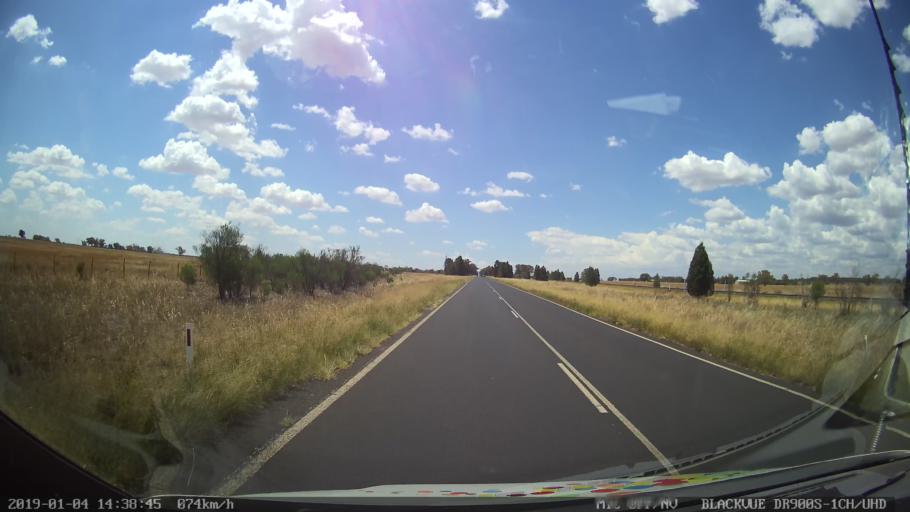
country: AU
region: New South Wales
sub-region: Dubbo Municipality
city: Dubbo
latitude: -32.1727
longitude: 148.6316
